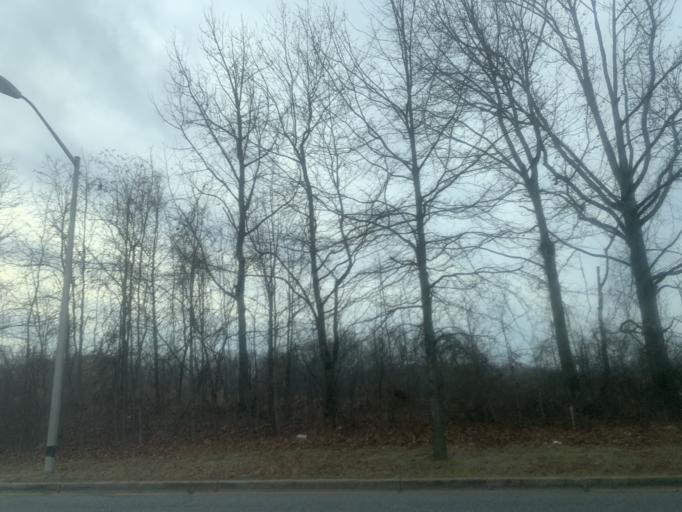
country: US
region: Maryland
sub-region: Prince George's County
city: Forestville
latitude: 38.8298
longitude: -76.8532
